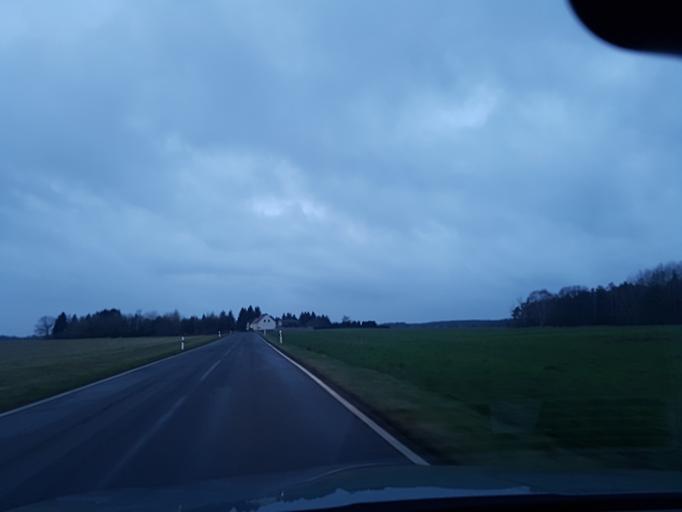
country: DE
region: Brandenburg
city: Schilda
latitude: 51.6031
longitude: 13.4077
